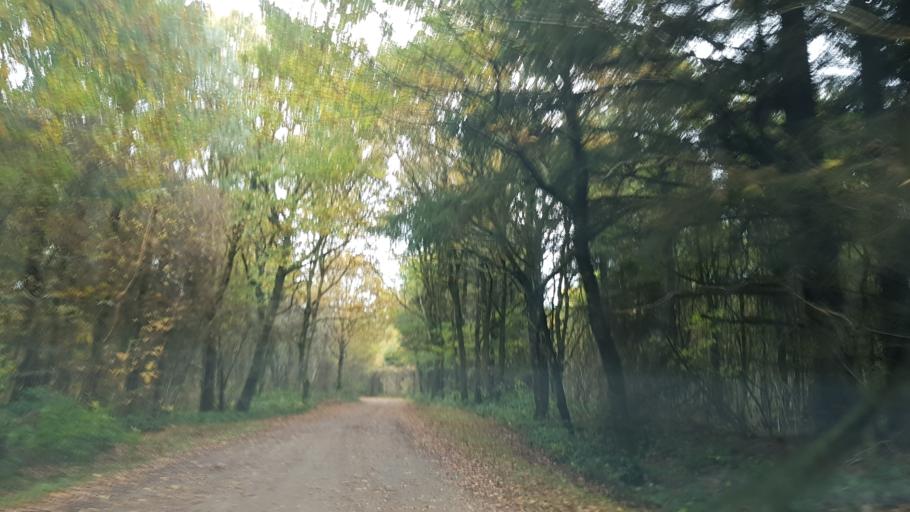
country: DK
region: South Denmark
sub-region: Tonder Kommune
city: Sherrebek
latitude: 55.1733
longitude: 8.7651
